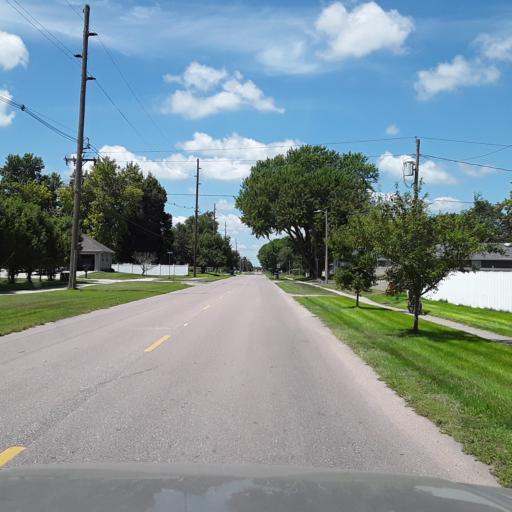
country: US
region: Nebraska
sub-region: Merrick County
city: Central City
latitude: 41.1048
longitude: -98.0061
